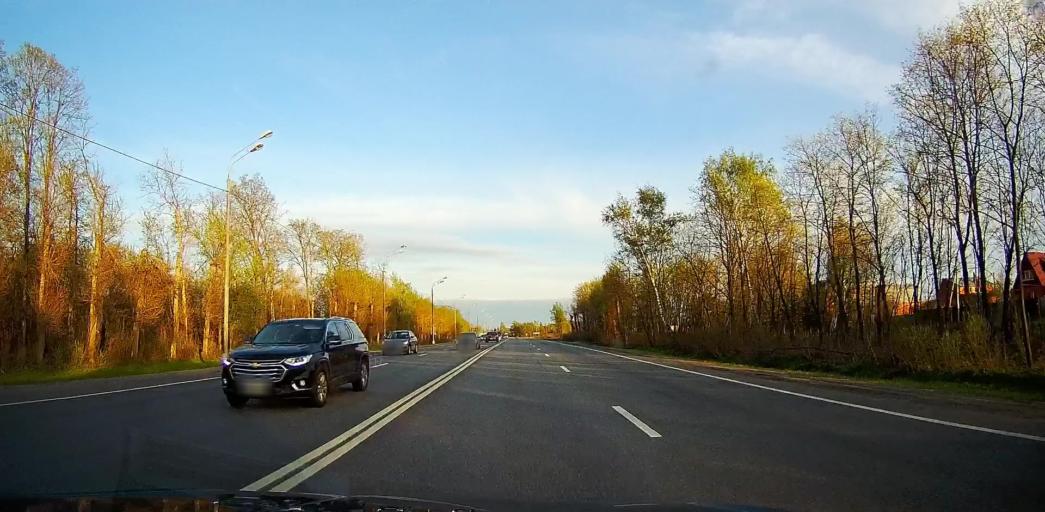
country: RU
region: Moskovskaya
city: Troitskoye
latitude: 55.2577
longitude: 38.5146
